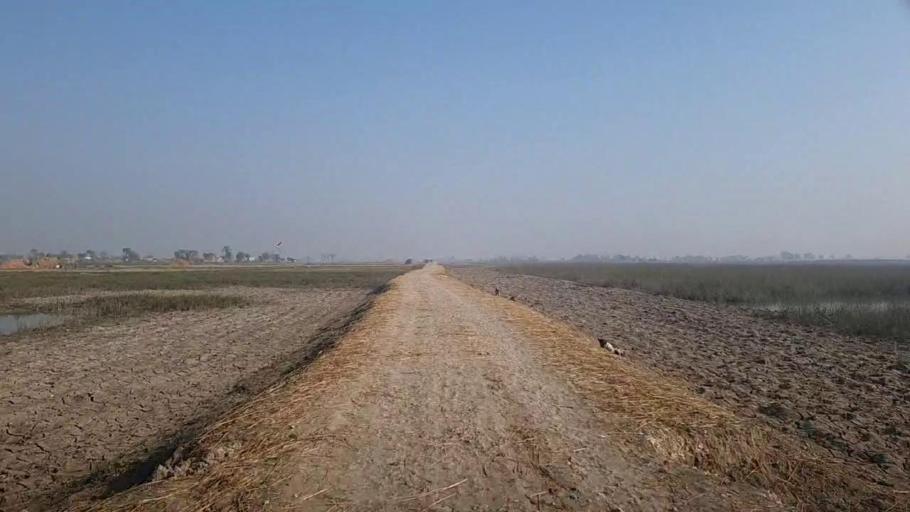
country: PK
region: Sindh
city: Radhan
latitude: 27.1400
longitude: 67.9074
